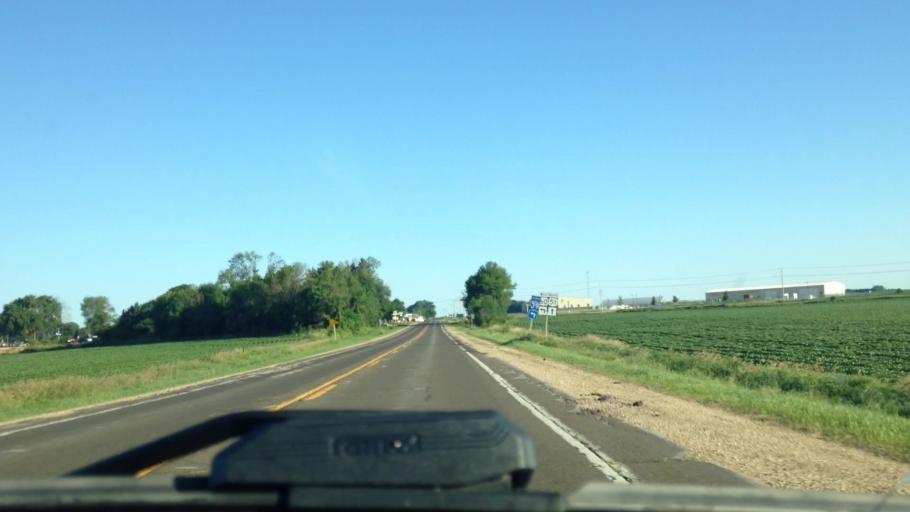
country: US
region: Wisconsin
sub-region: Columbia County
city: Poynette
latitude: 43.3346
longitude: -89.3645
